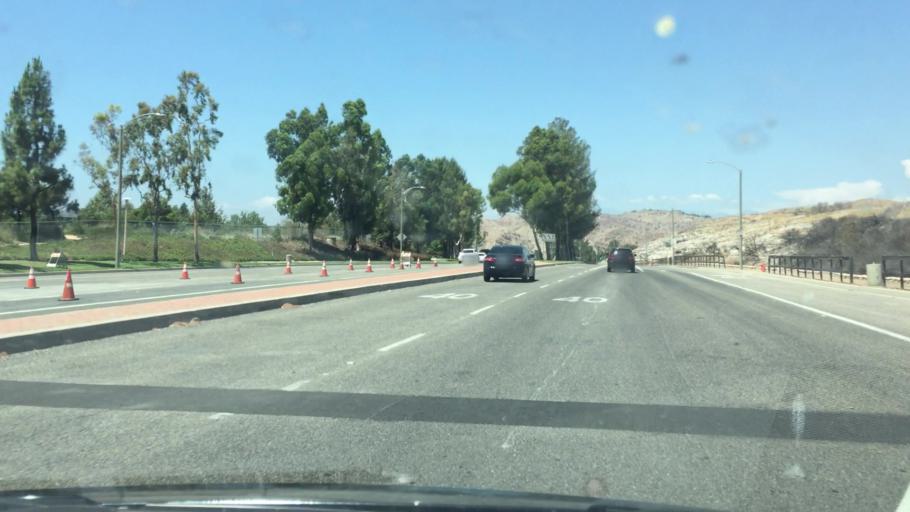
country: US
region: California
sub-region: Orange County
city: North Tustin
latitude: 33.7927
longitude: -117.7612
